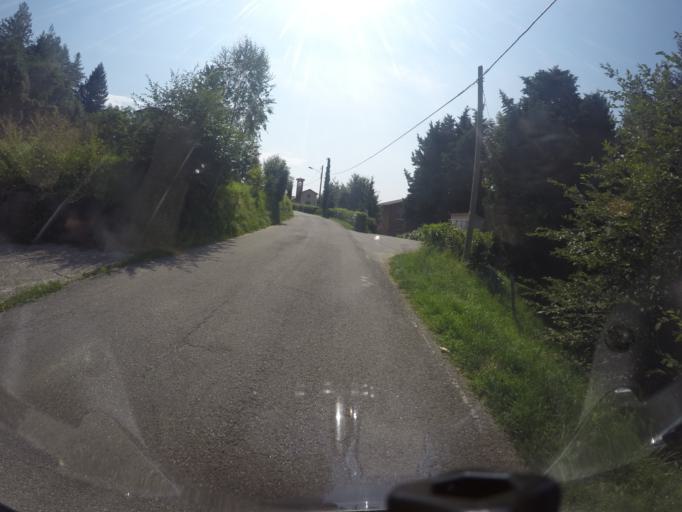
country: IT
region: Lombardy
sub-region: Provincia di Lecco
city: Santa Maria Hoe
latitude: 45.7524
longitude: 9.3854
